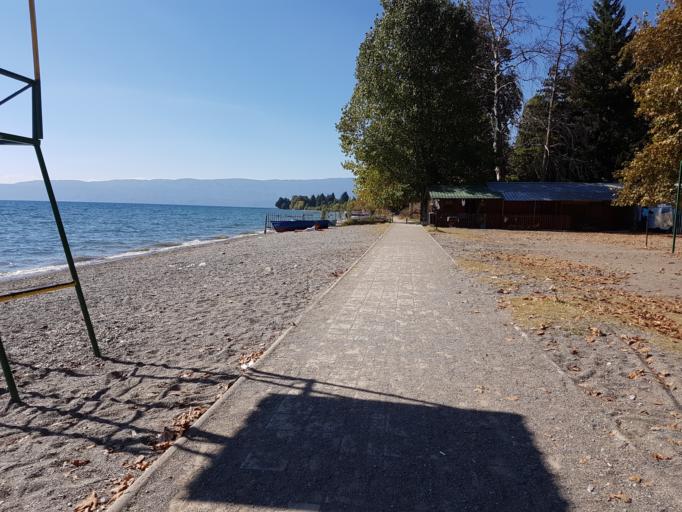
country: MK
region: Ohrid
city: Ohrid
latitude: 41.1198
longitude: 20.7828
